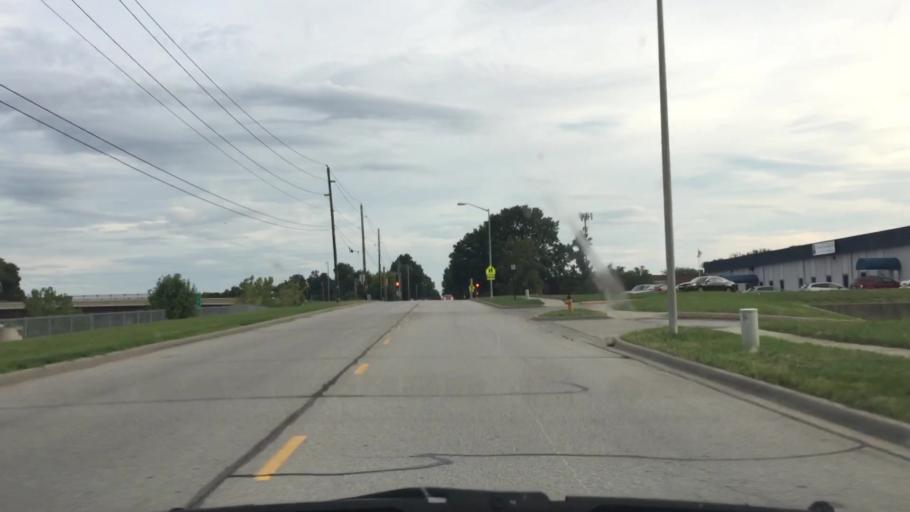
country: US
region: Kansas
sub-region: Johnson County
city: Lenexa
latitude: 38.9653
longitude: -94.7143
